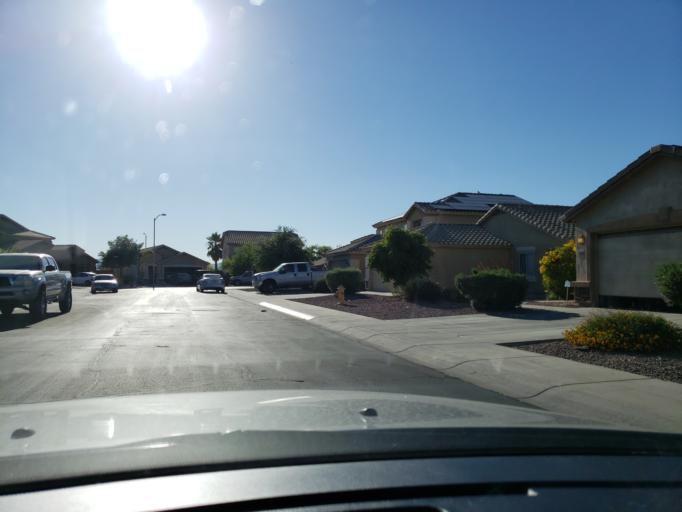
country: US
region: Arizona
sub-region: Maricopa County
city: Youngtown
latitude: 33.5694
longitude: -112.3099
